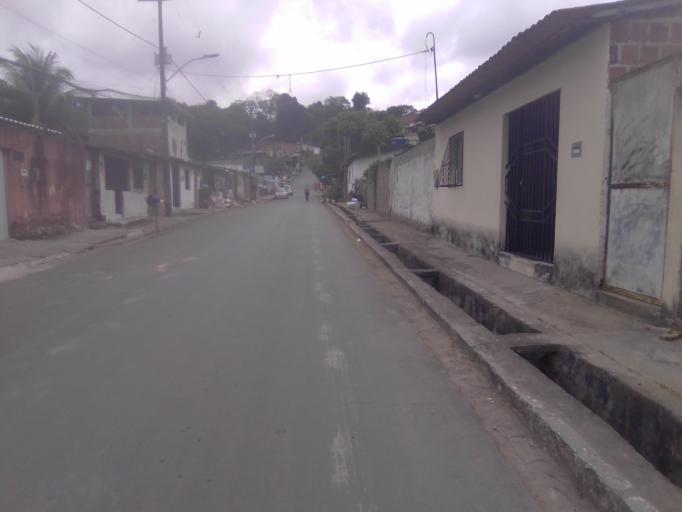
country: BR
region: Pernambuco
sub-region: Jaboatao Dos Guararapes
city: Jaboatao dos Guararapes
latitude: -8.0658
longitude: -35.0012
